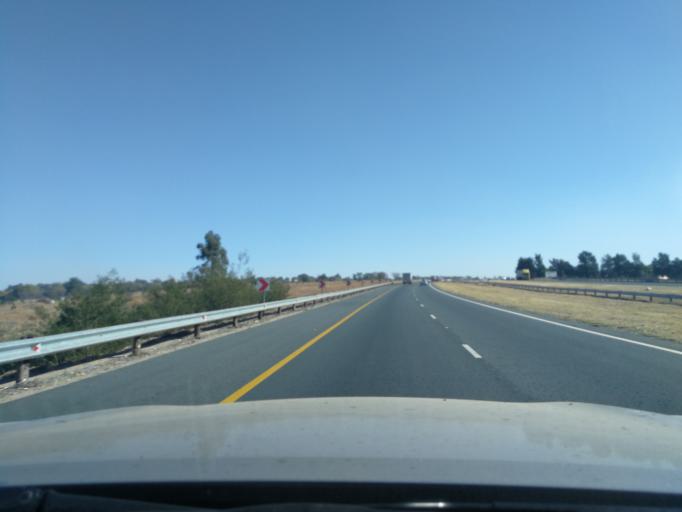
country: ZA
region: Gauteng
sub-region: West Rand District Municipality
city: Muldersdriseloop
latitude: -26.0057
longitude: 27.8969
